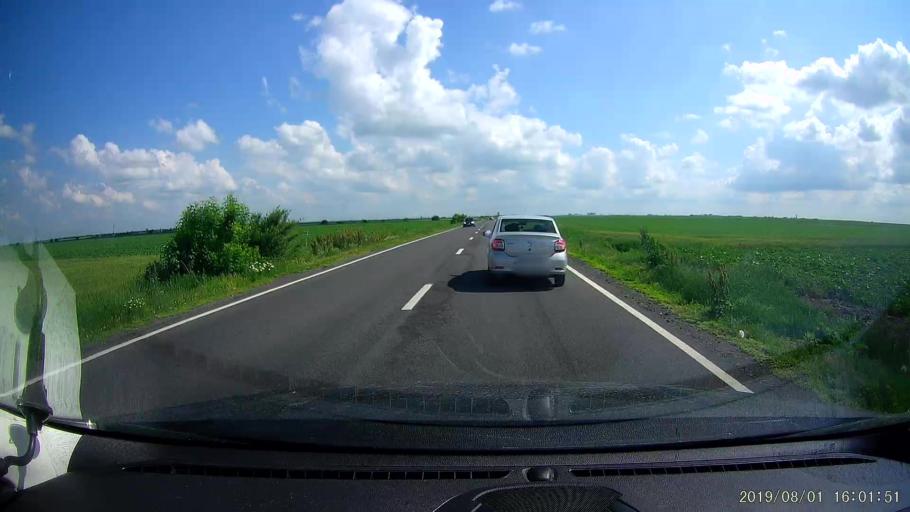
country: RO
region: Ialomita
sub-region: Comuna Ciulnita
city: Ciulnita
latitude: 44.5009
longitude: 27.3892
